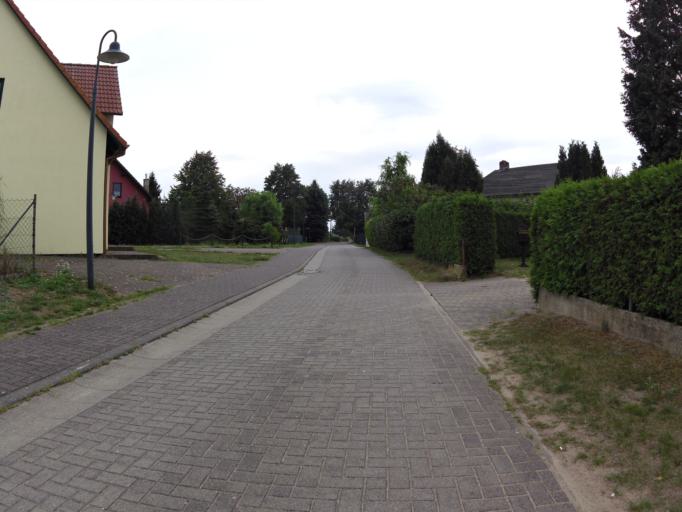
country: DE
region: Mecklenburg-Vorpommern
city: Seebad Heringsdorf
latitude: 53.8801
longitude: 14.1692
